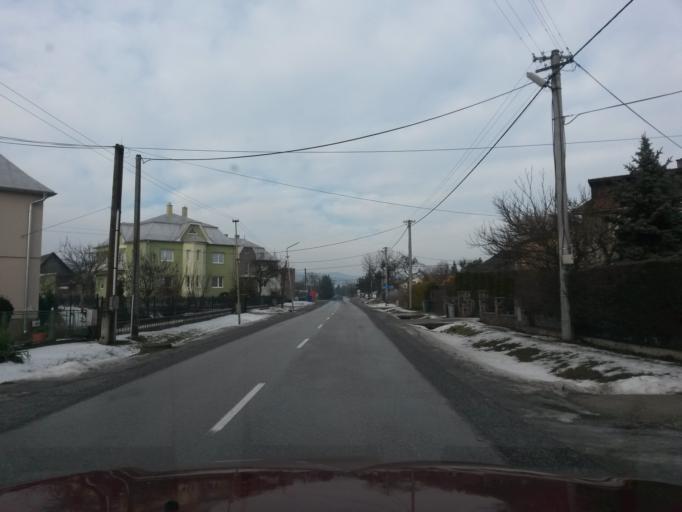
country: SK
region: Kosicky
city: Kosice
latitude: 48.7813
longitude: 21.3276
